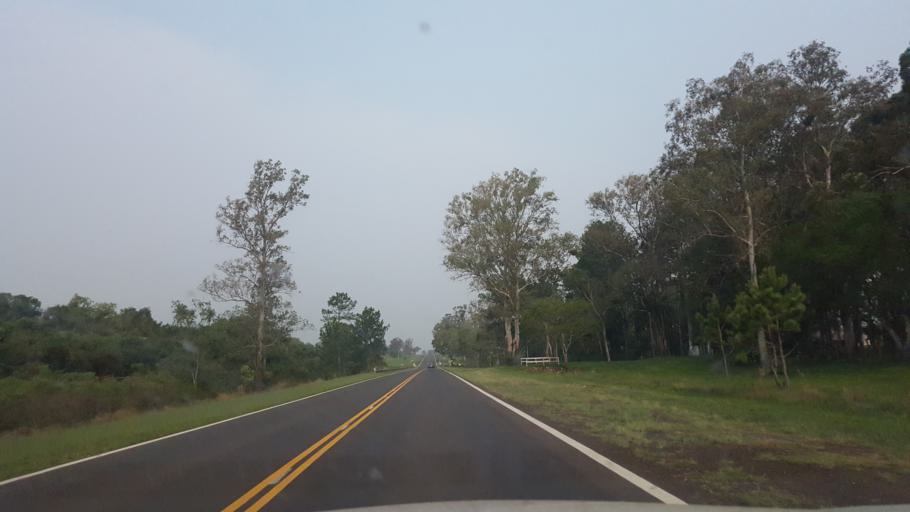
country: AR
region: Corrientes
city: Ita Ibate
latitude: -27.5119
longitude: -57.2361
